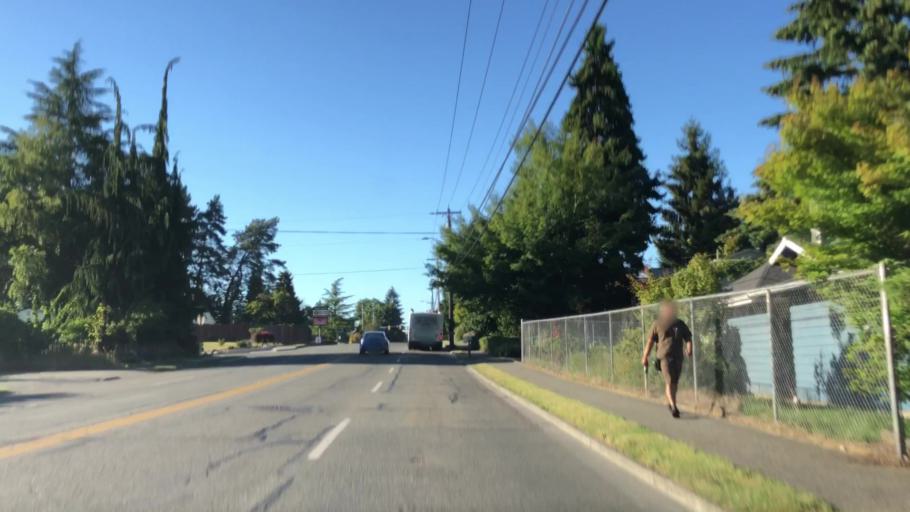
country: US
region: Washington
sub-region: Snohomish County
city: Mountlake Terrace
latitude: 47.7946
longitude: -122.2923
